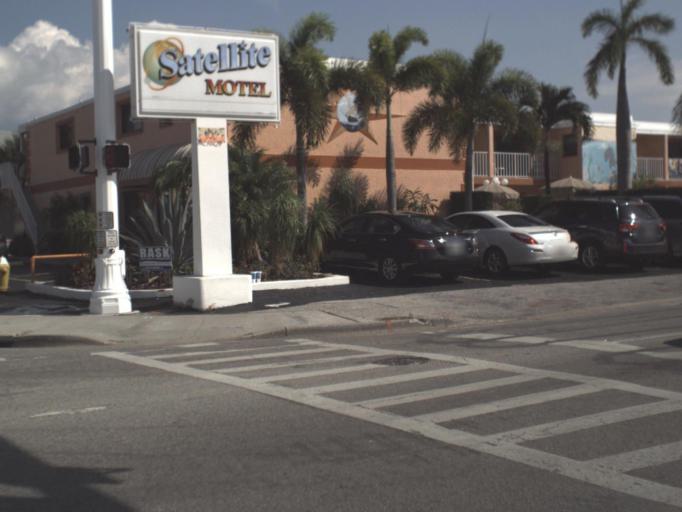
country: US
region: Florida
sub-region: Pinellas County
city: Treasure Island
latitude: 27.7722
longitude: -82.7721
